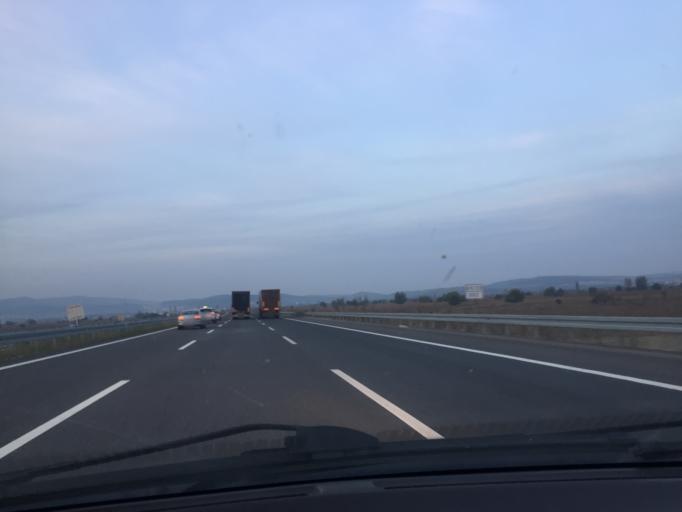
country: TR
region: Manisa
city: Halitpasa
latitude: 38.7469
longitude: 27.6595
